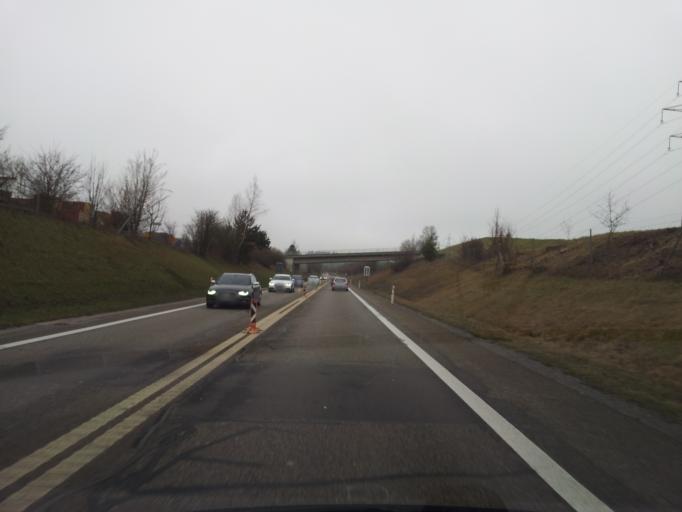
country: CH
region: Zurich
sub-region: Bezirk Winterthur
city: Hettlingen
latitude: 47.5381
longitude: 8.6921
